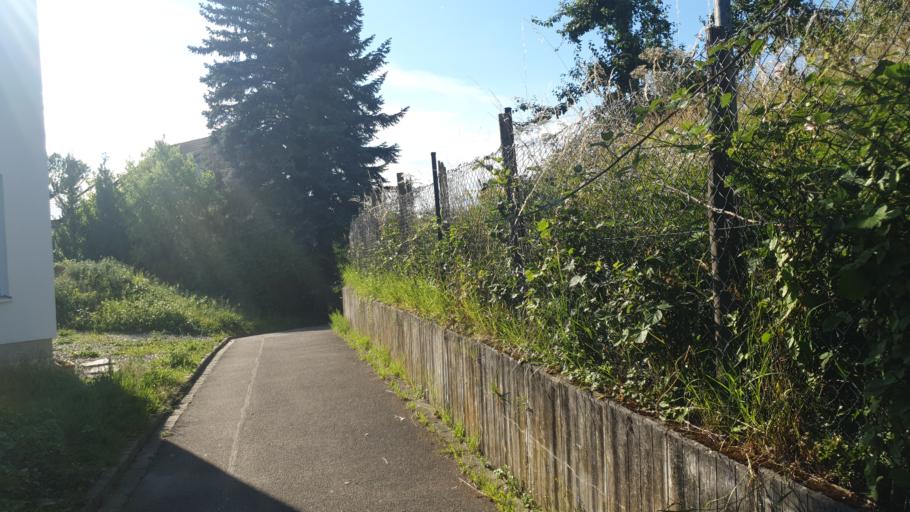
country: DE
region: Baden-Wuerttemberg
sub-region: Freiburg Region
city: Merzhausen
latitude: 47.9720
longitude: 7.8336
